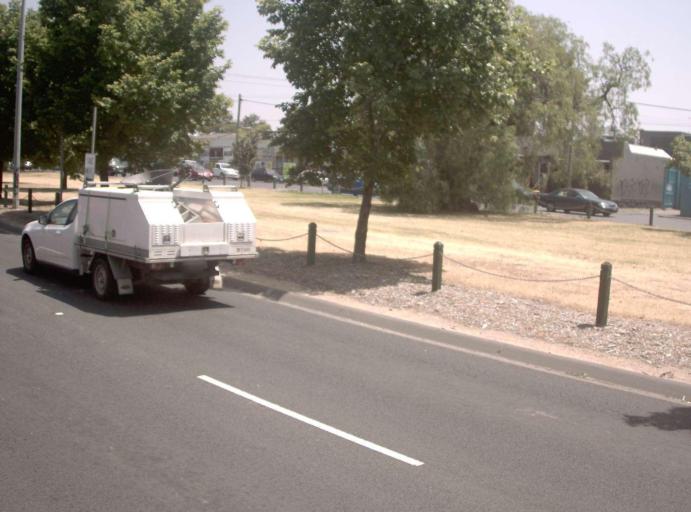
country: AU
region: Victoria
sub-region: Yarra
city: Clifton Hill
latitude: -37.7945
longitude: 144.9893
